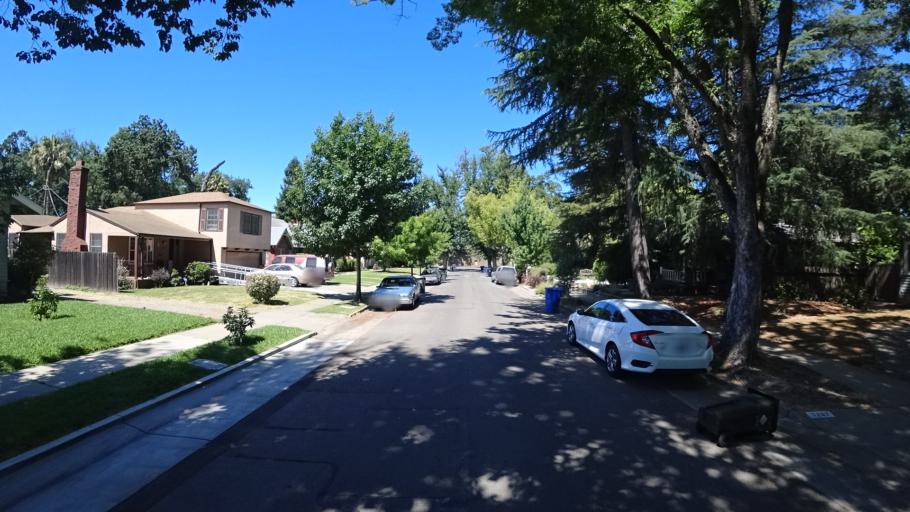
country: US
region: California
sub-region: Sacramento County
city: Sacramento
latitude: 38.5428
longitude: -121.4719
